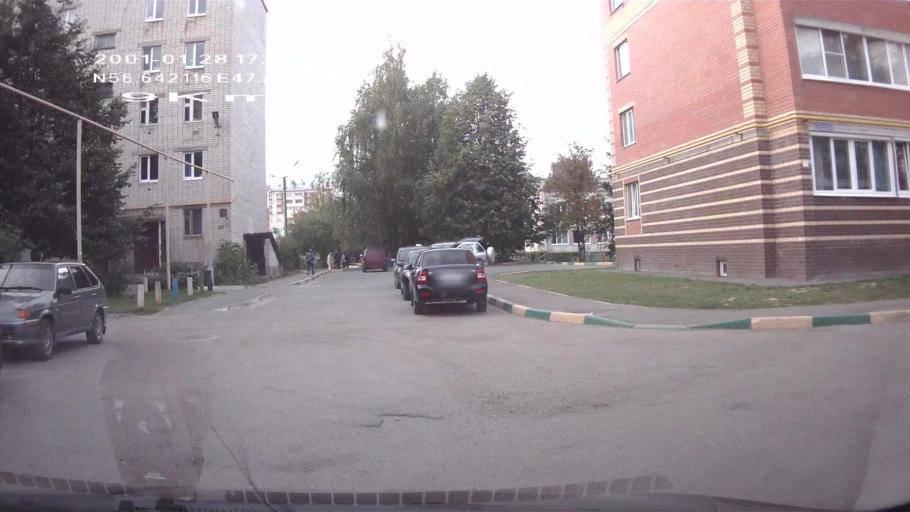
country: RU
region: Mariy-El
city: Medvedevo
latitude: 56.6421
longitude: 47.8411
